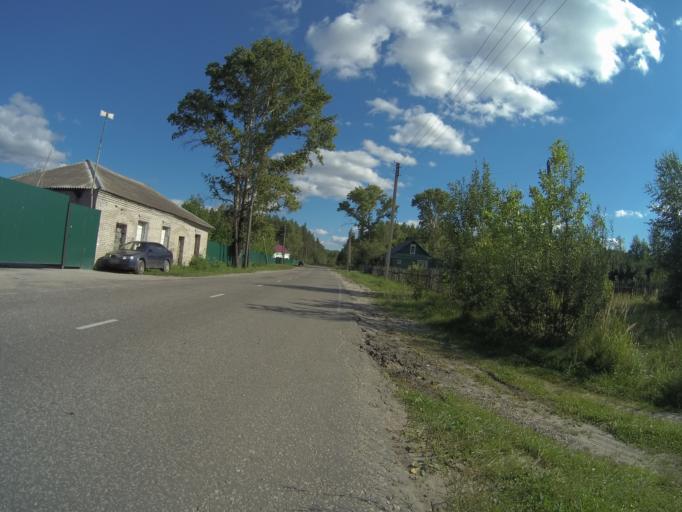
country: RU
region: Vladimir
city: Urshel'skiy
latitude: 55.6698
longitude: 40.2231
